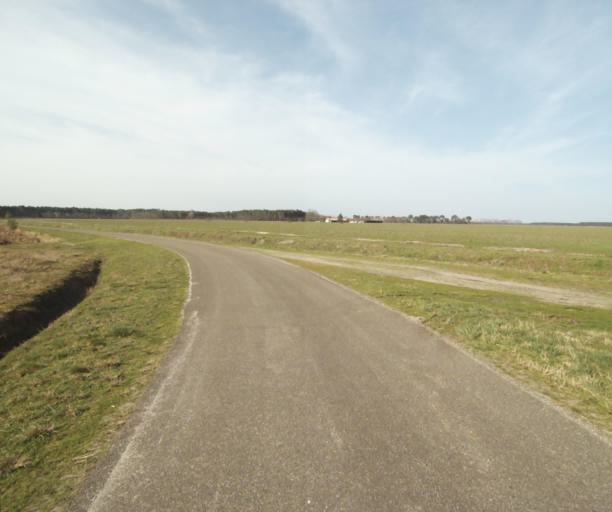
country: FR
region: Aquitaine
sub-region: Departement des Landes
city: Sarbazan
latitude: 44.1406
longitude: -0.1550
